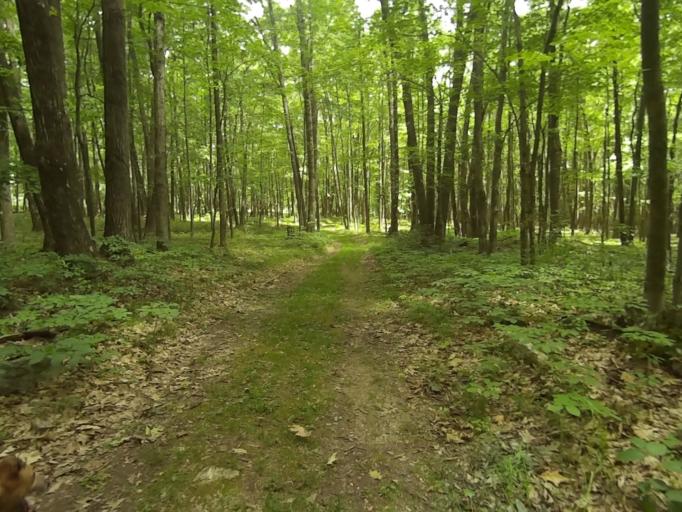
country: US
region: Pennsylvania
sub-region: Centre County
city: Stormstown
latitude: 40.9136
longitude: -78.0556
